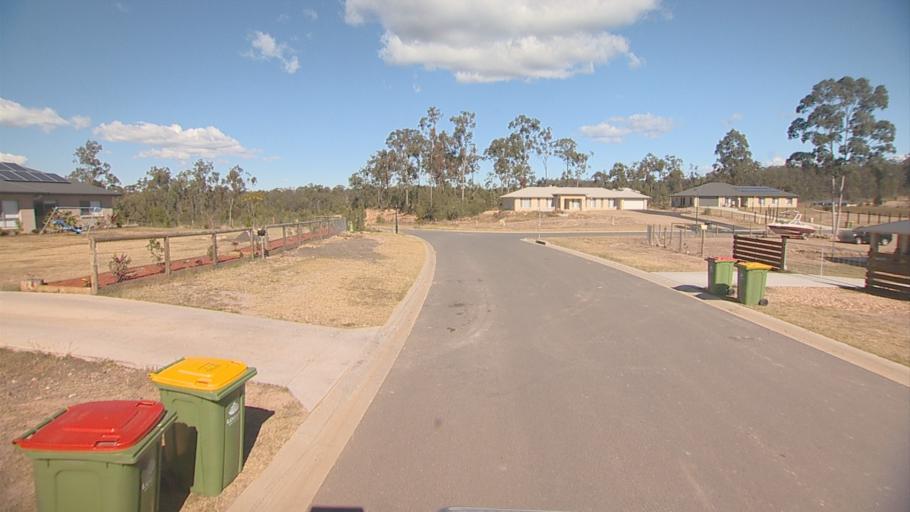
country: AU
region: Queensland
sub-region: Logan
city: North Maclean
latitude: -27.7593
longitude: 152.9340
